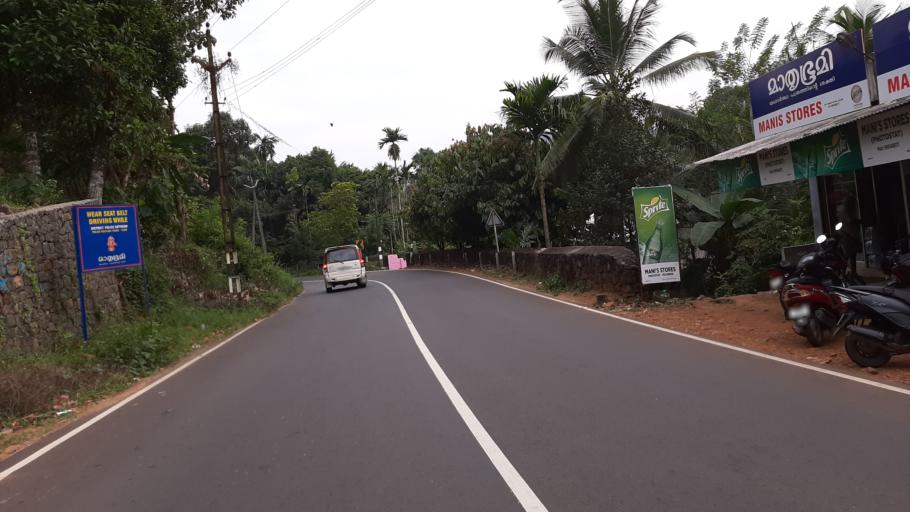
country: IN
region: Kerala
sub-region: Pattanamtitta
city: Pathanamthitta
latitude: 9.4541
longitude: 76.8672
